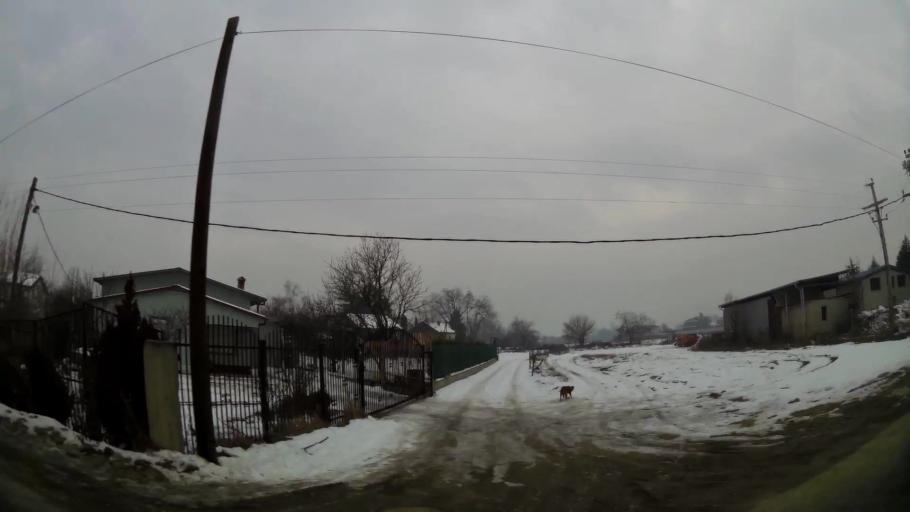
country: MK
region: Cucer-Sandevo
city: Chucher - Sandevo
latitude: 42.0480
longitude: 21.3659
